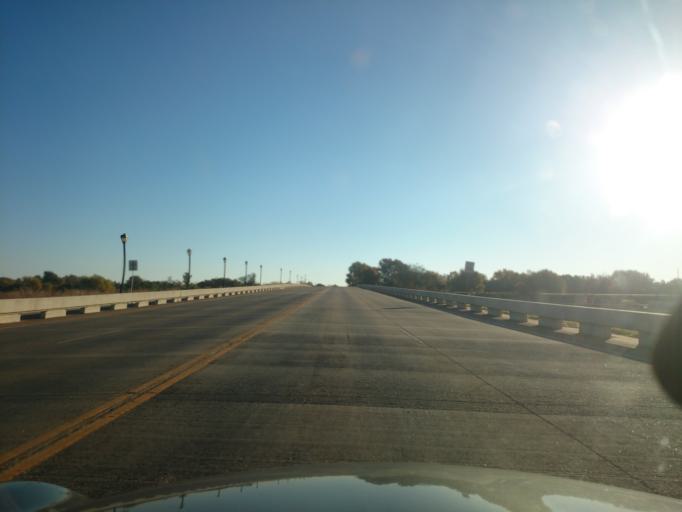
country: US
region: Oklahoma
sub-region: Payne County
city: Stillwater
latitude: 36.1451
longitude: -97.0652
